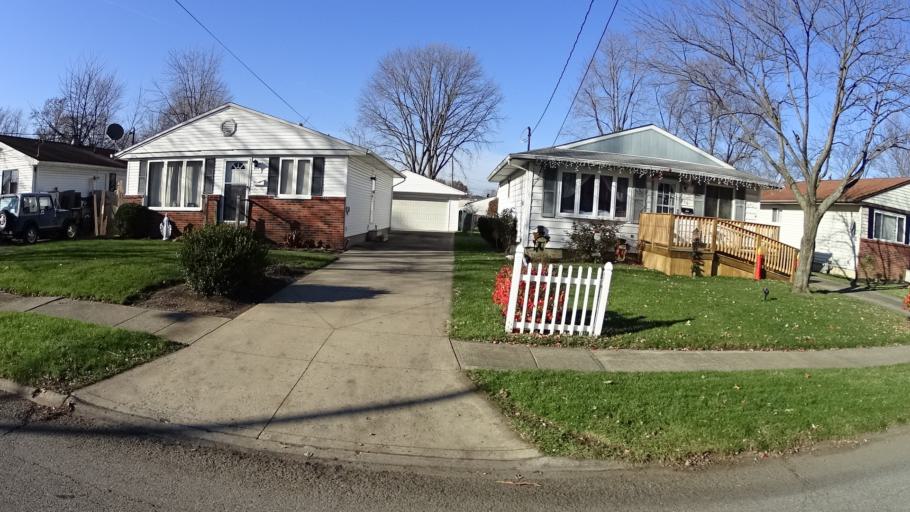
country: US
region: Ohio
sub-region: Lorain County
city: Elyria
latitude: 41.3886
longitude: -82.0750
